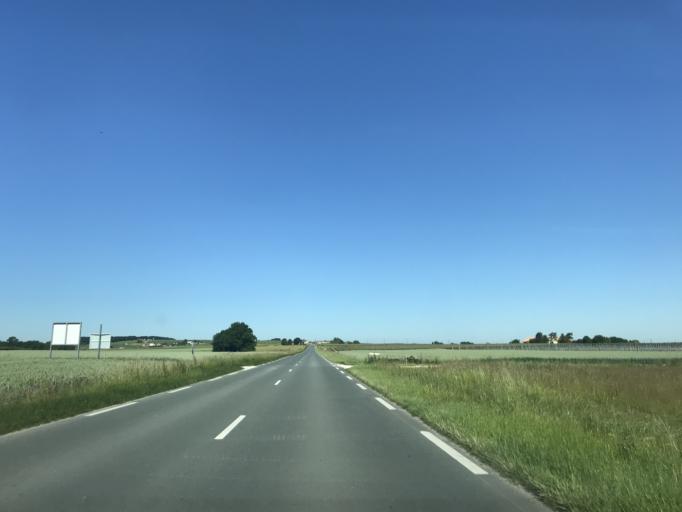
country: FR
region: Poitou-Charentes
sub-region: Departement de la Charente
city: Segonzac
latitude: 45.5323
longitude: -0.3132
